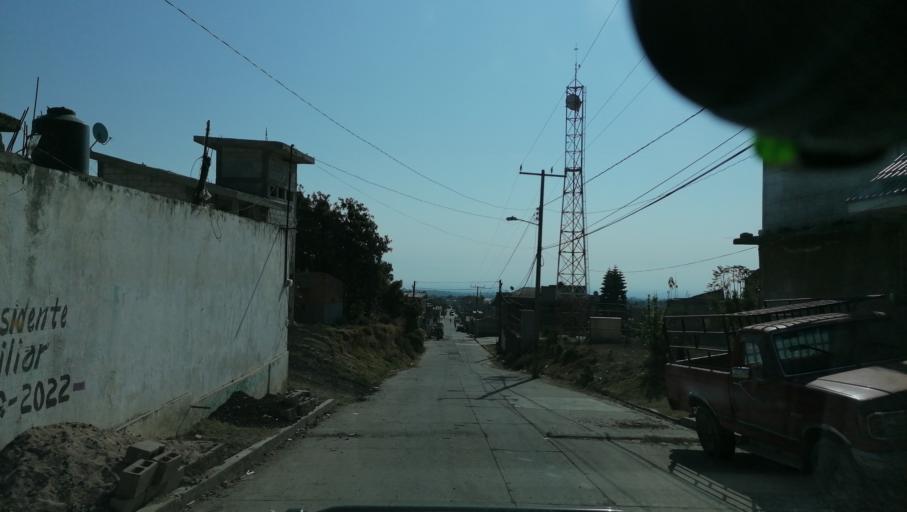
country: MX
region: Puebla
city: Domingo Arenas
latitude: 19.1358
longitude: -98.4951
